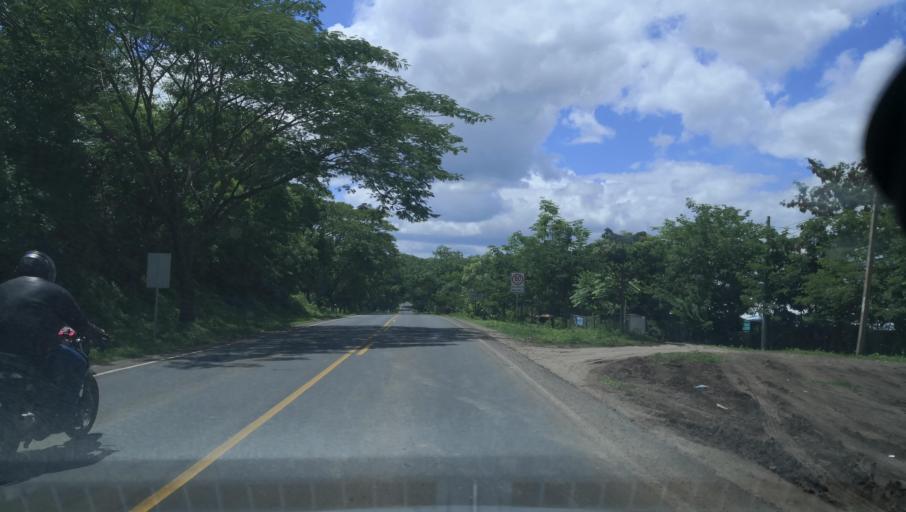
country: NI
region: Esteli
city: Condega
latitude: 13.3804
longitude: -86.4016
